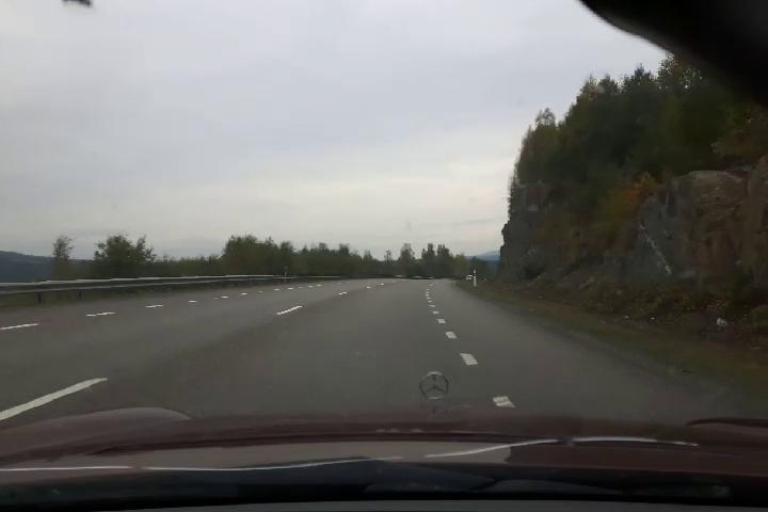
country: SE
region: Vaesternorrland
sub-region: Kramfors Kommun
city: Nordingra
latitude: 63.0054
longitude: 18.2335
